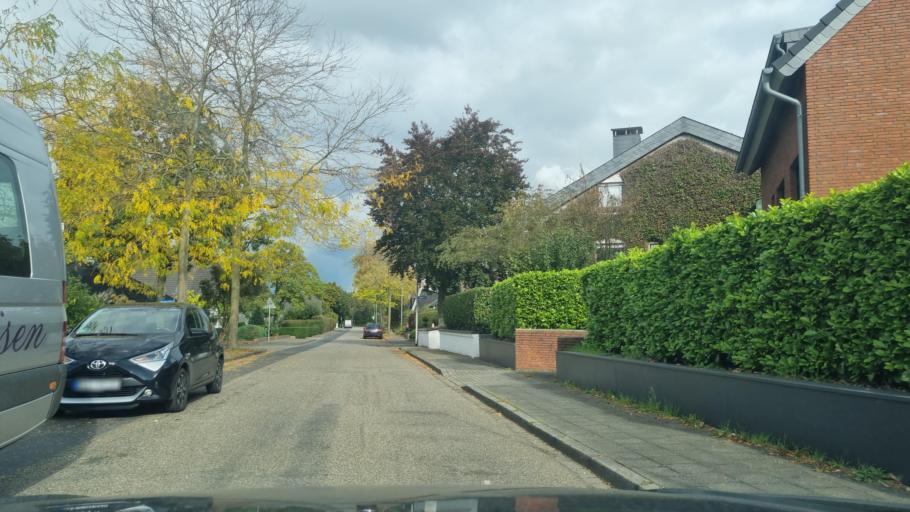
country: DE
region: North Rhine-Westphalia
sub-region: Regierungsbezirk Dusseldorf
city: Kleve
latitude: 51.7808
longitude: 6.1039
